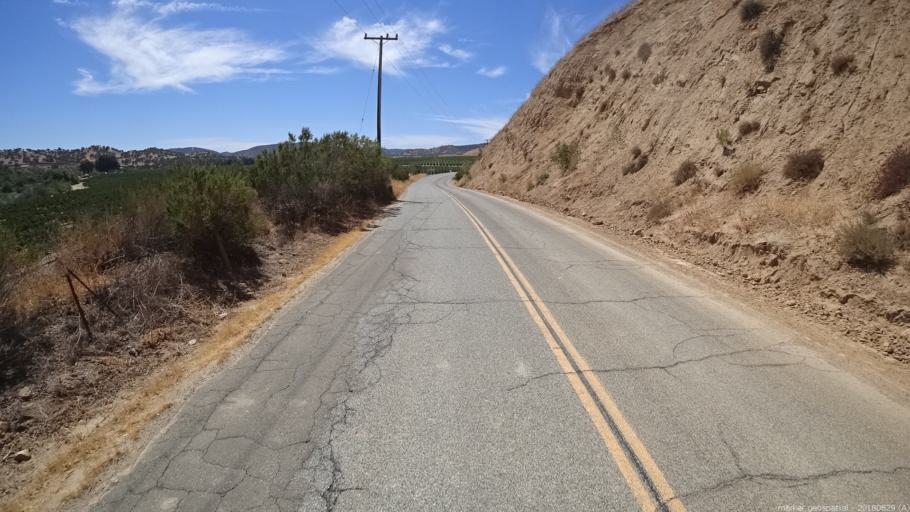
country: US
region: California
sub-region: San Luis Obispo County
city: Lake Nacimiento
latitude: 35.8189
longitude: -120.8425
